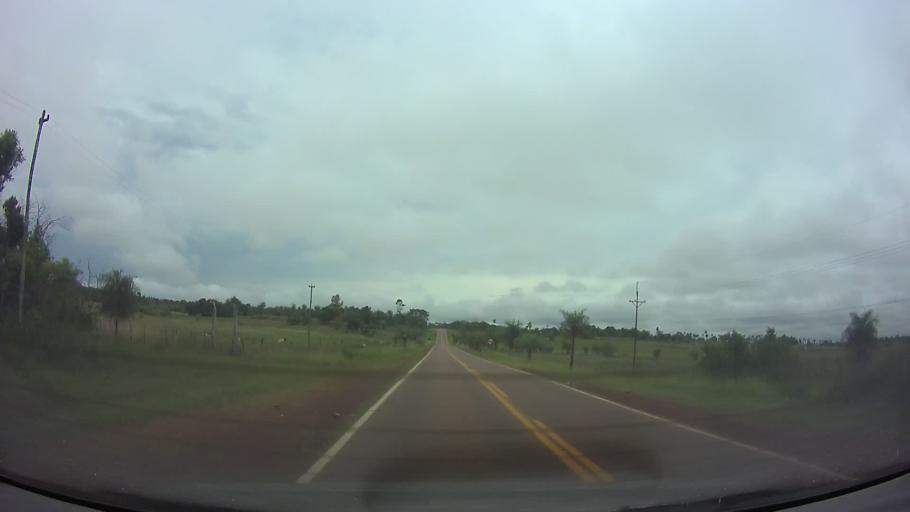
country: PY
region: Paraguari
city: Acahay
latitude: -25.8787
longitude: -57.1232
